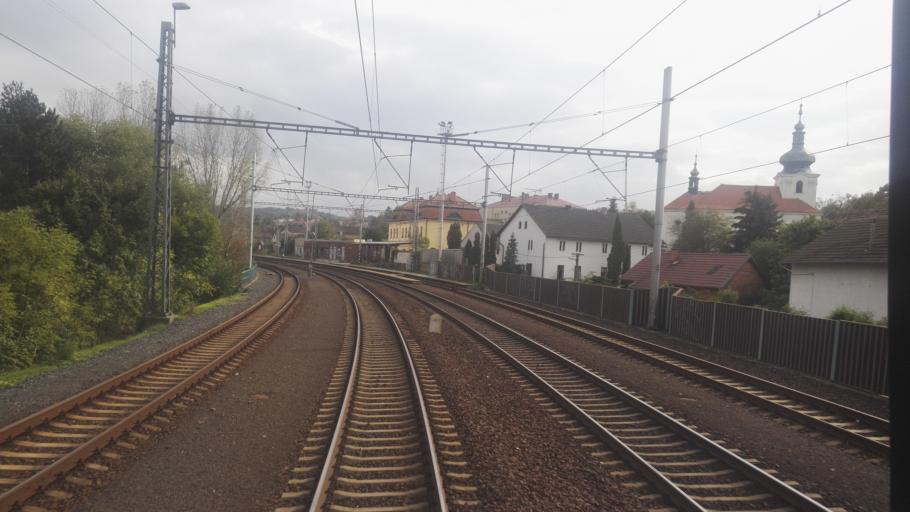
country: CZ
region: Central Bohemia
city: Libcice nad Vltavou
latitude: 50.2011
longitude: 14.3632
